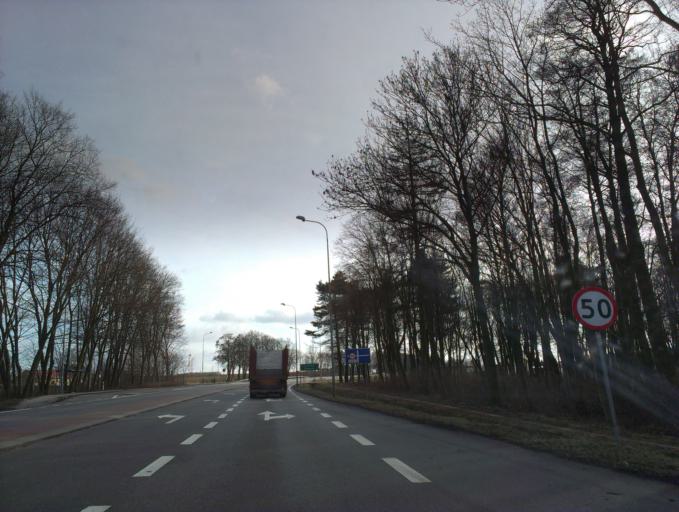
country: PL
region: Kujawsko-Pomorskie
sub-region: Powiat lipnowski
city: Lipno
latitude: 52.8721
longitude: 19.1514
